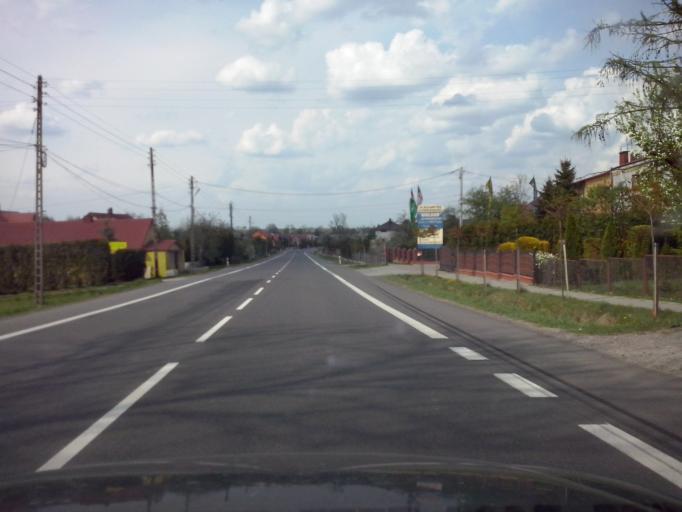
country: PL
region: Subcarpathian Voivodeship
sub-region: Powiat rzeszowski
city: Kamien
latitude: 50.3101
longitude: 22.1313
